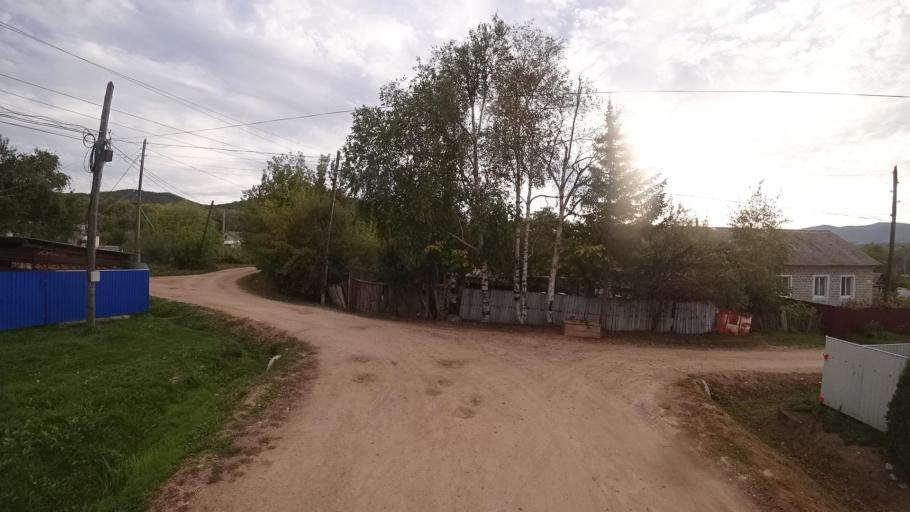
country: RU
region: Primorskiy
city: Yakovlevka
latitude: 44.4140
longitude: 133.4500
